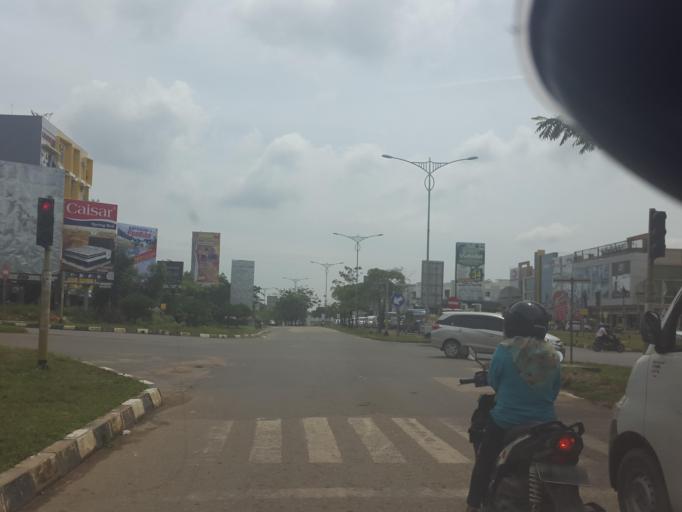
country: SG
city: Singapore
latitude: 1.1150
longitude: 104.0583
